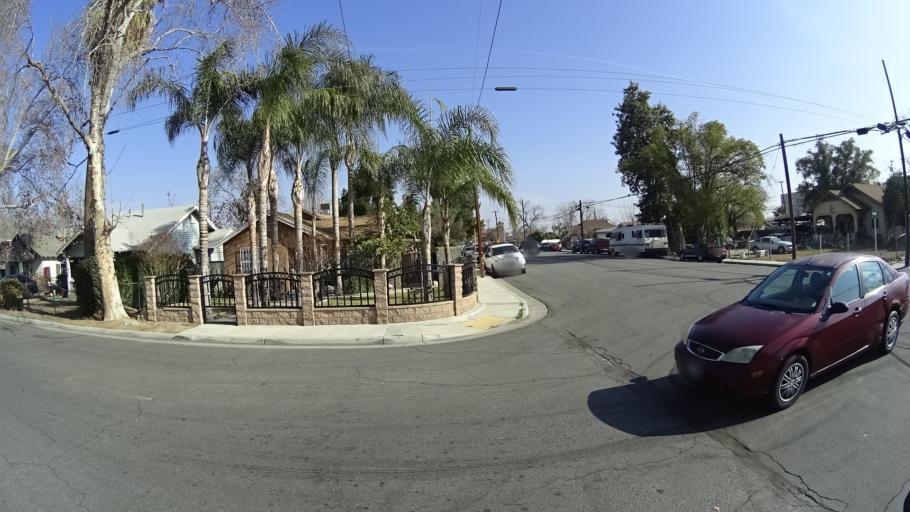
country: US
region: California
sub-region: Kern County
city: Bakersfield
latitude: 35.3629
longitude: -119.0096
